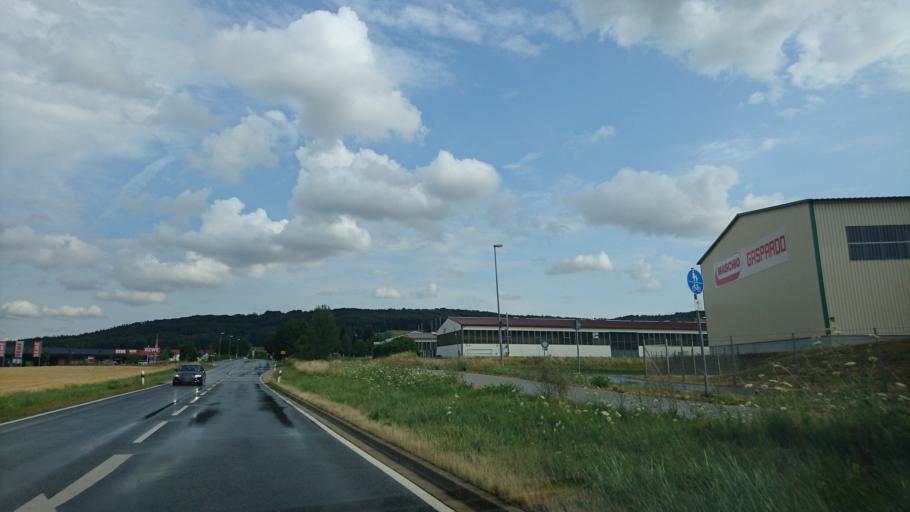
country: DE
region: Bavaria
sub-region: Regierungsbezirk Mittelfranken
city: Thalmassing
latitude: 49.0926
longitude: 11.2121
